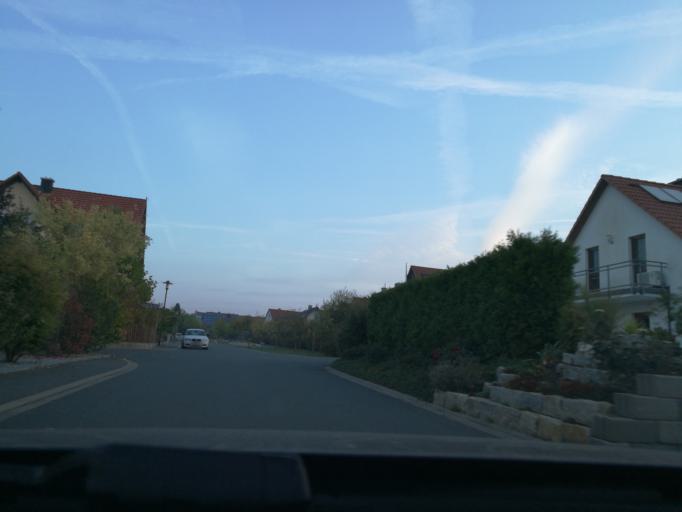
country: DE
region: Bavaria
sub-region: Regierungsbezirk Mittelfranken
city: Veitsbronn
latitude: 49.5101
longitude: 10.8937
